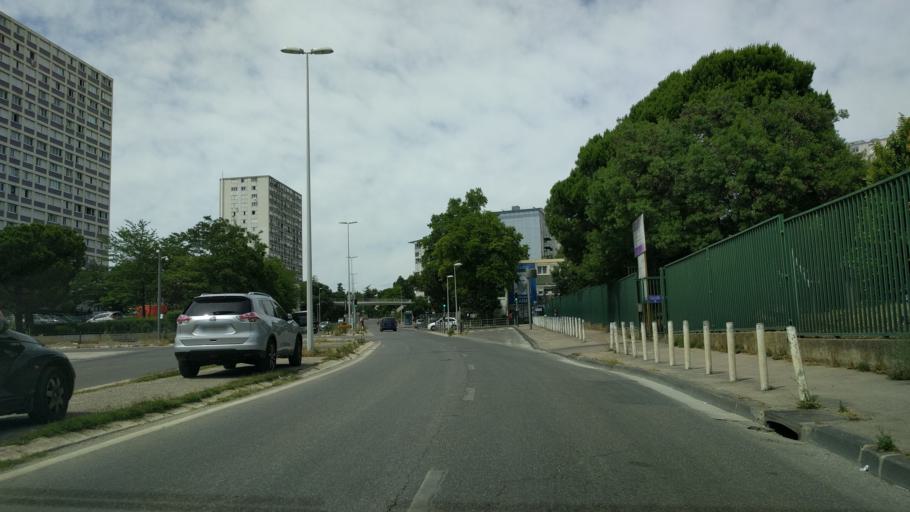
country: FR
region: Provence-Alpes-Cote d'Azur
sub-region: Departement des Bouches-du-Rhone
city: Marseille 13
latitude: 43.3328
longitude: 5.3992
